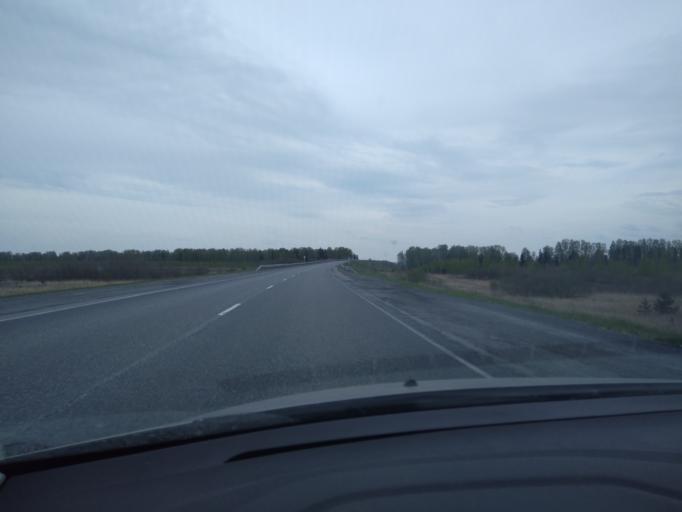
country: RU
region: Sverdlovsk
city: Kamyshlov
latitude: 56.8592
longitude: 62.8008
